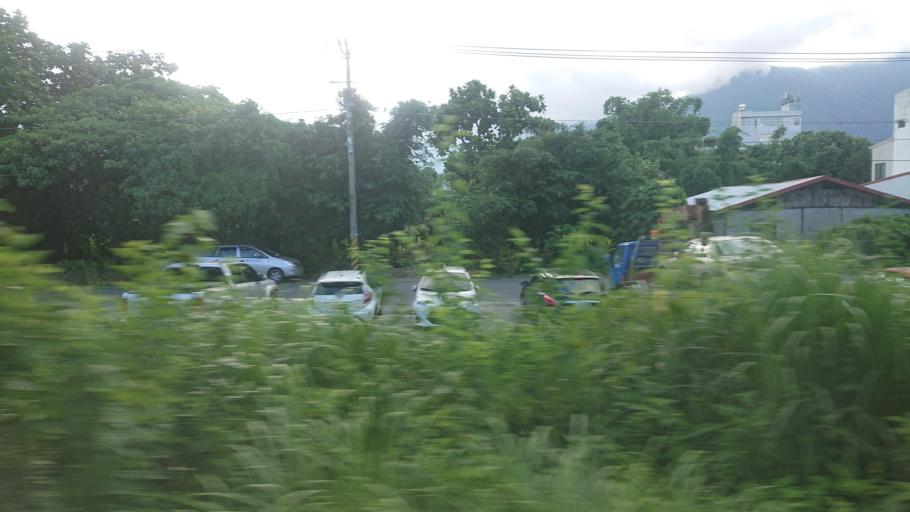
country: TW
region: Taiwan
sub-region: Hualien
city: Hualian
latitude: 23.9836
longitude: 121.5963
